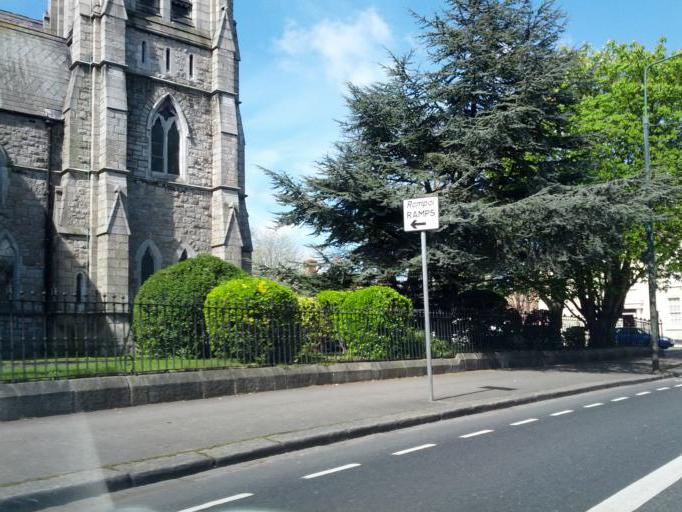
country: IE
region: Leinster
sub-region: Dublin City
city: Dublin
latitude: 53.3303
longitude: -6.2516
